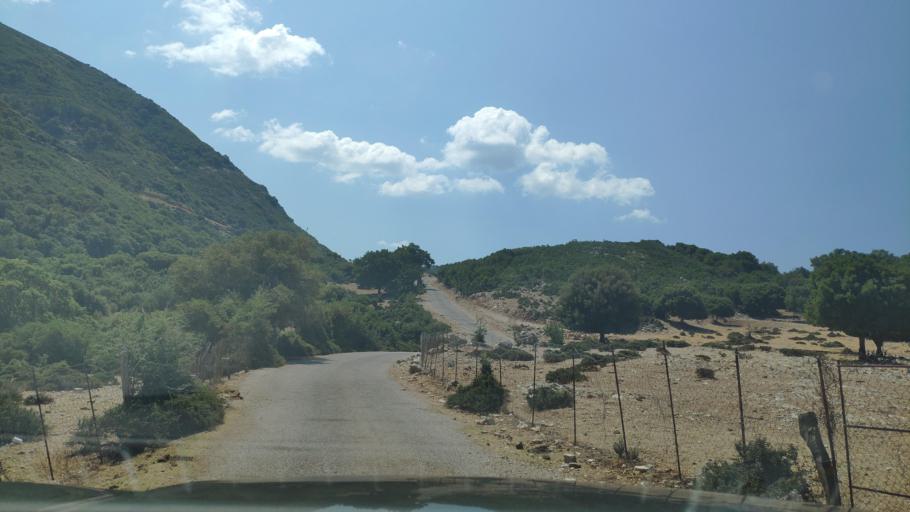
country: GR
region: West Greece
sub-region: Nomos Aitolias kai Akarnanias
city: Monastirakion
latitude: 38.8199
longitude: 20.9329
